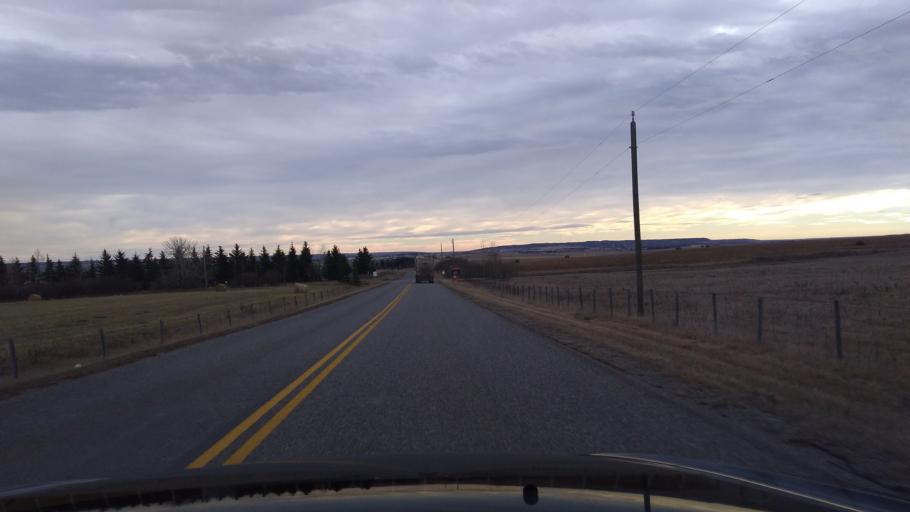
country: CA
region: Alberta
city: Cochrane
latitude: 51.0959
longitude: -114.4456
